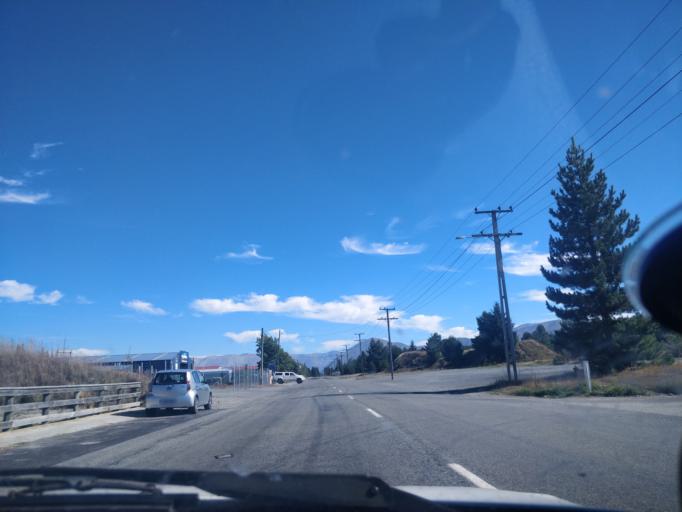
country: NZ
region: Otago
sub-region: Queenstown-Lakes District
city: Wanaka
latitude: -44.2644
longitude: 170.0925
